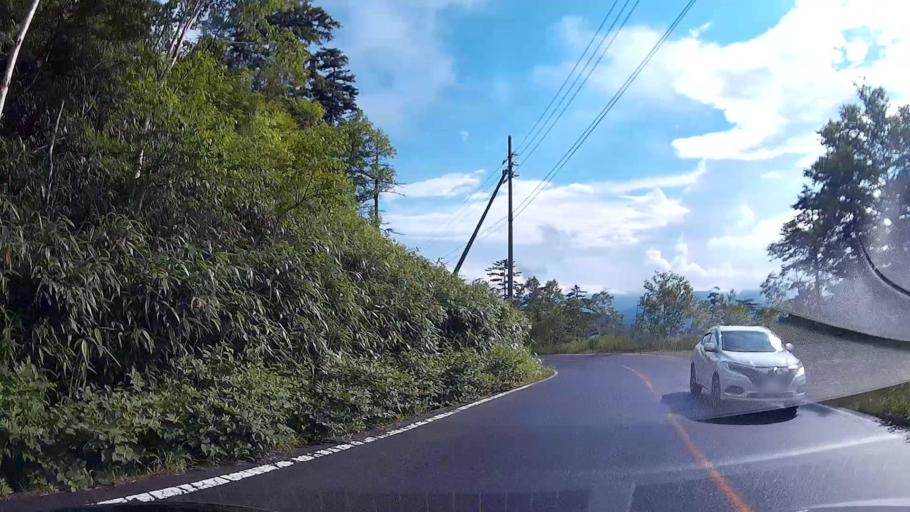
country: JP
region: Nagano
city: Nakano
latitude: 36.6390
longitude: 138.5247
